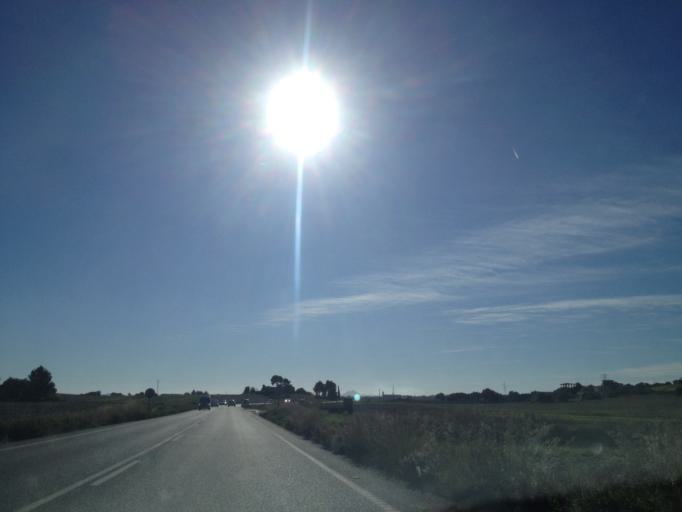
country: ES
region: Balearic Islands
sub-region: Illes Balears
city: Ariany
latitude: 39.6423
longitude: 3.1005
